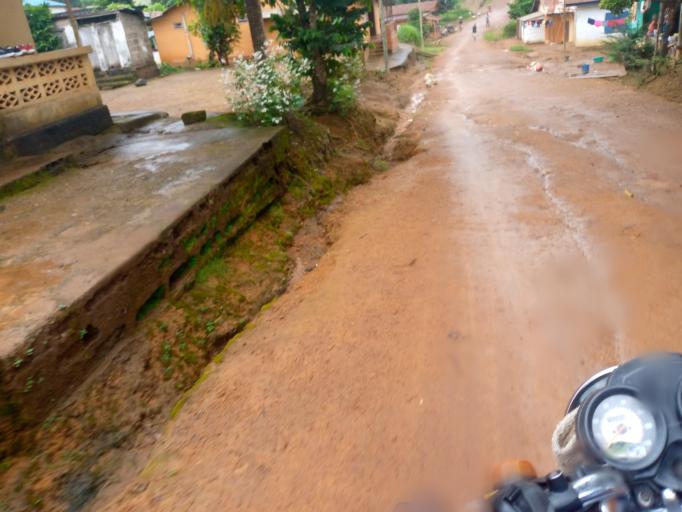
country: SL
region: Eastern Province
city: Kenema
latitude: 7.8738
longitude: -11.1786
